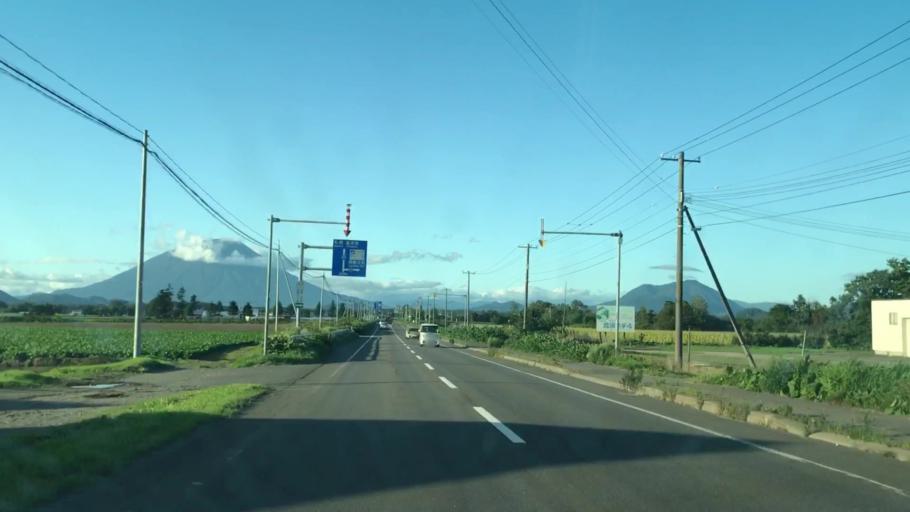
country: JP
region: Hokkaido
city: Date
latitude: 42.6396
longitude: 140.8026
